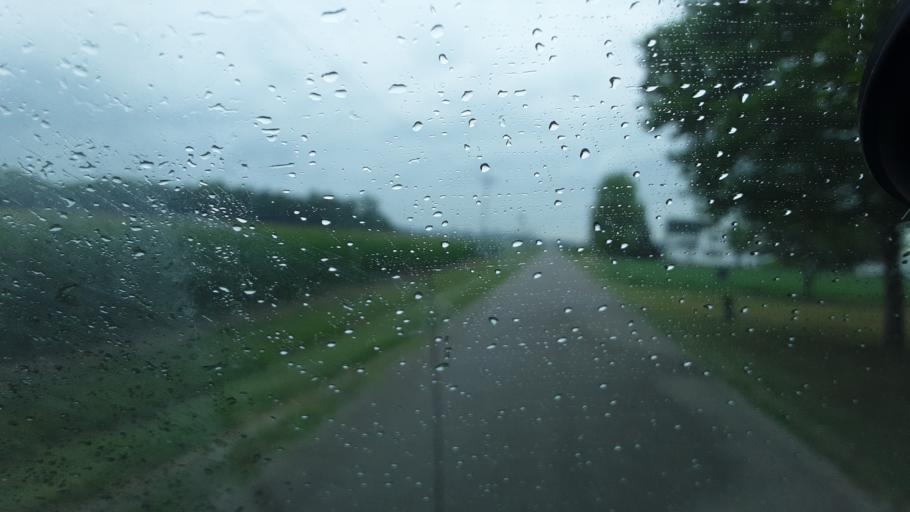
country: US
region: Ohio
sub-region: Defiance County
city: Hicksville
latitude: 41.3129
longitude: -84.6696
